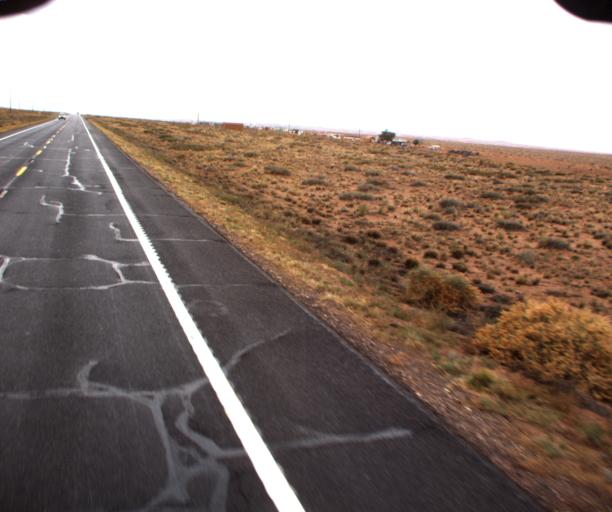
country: US
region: Arizona
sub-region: Coconino County
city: Tuba City
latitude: 36.1474
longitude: -111.1426
